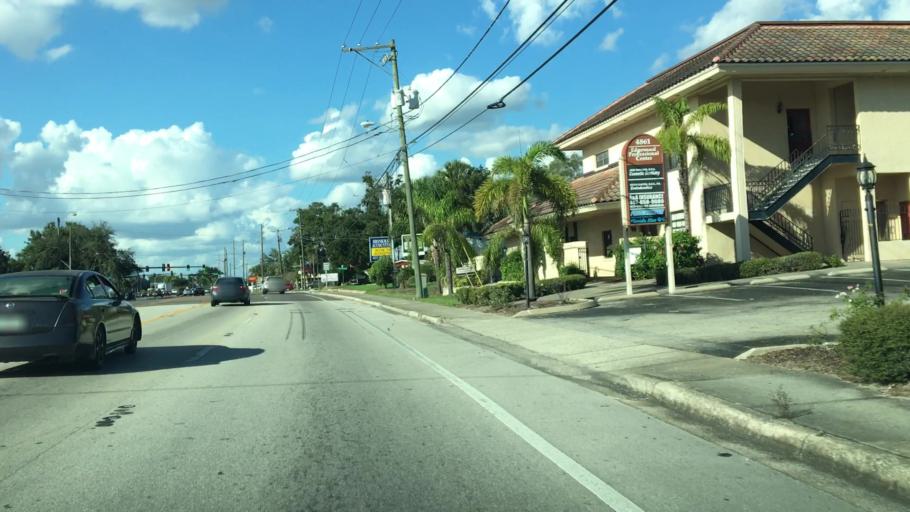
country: US
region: Florida
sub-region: Orange County
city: Edgewood
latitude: 28.4920
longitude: -81.3738
